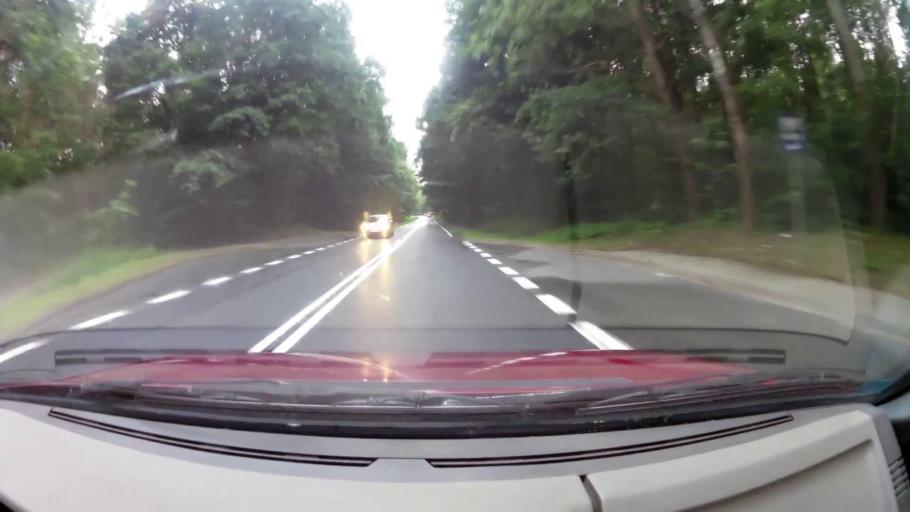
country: PL
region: West Pomeranian Voivodeship
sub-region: Powiat stargardzki
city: Chociwel
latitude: 53.4815
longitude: 15.3789
